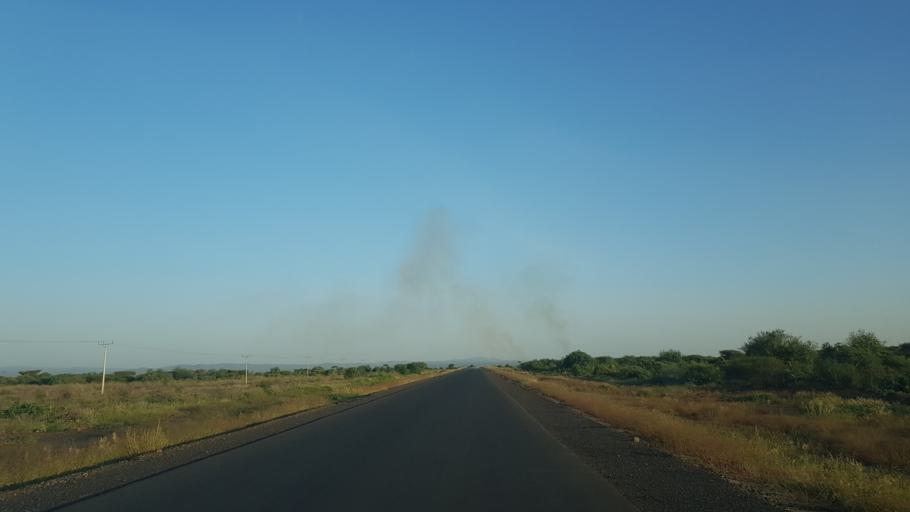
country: ET
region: Southern Nations, Nationalities, and People's Region
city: Lobuni
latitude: 5.1522
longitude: 36.1035
